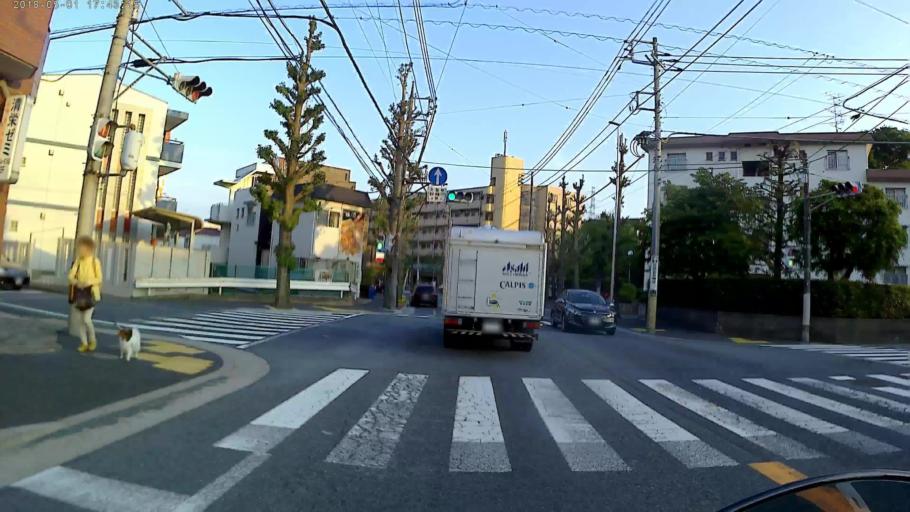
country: JP
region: Tokyo
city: Chofugaoka
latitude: 35.5740
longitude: 139.5771
